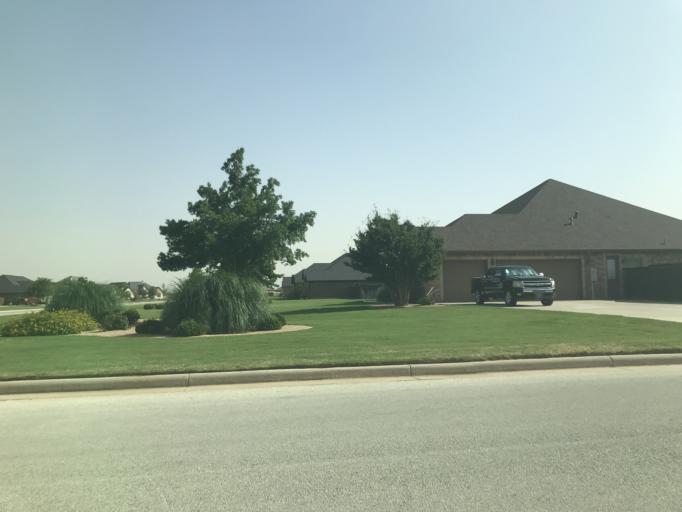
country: US
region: Texas
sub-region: Taylor County
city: Potosi
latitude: 32.3499
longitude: -99.7158
